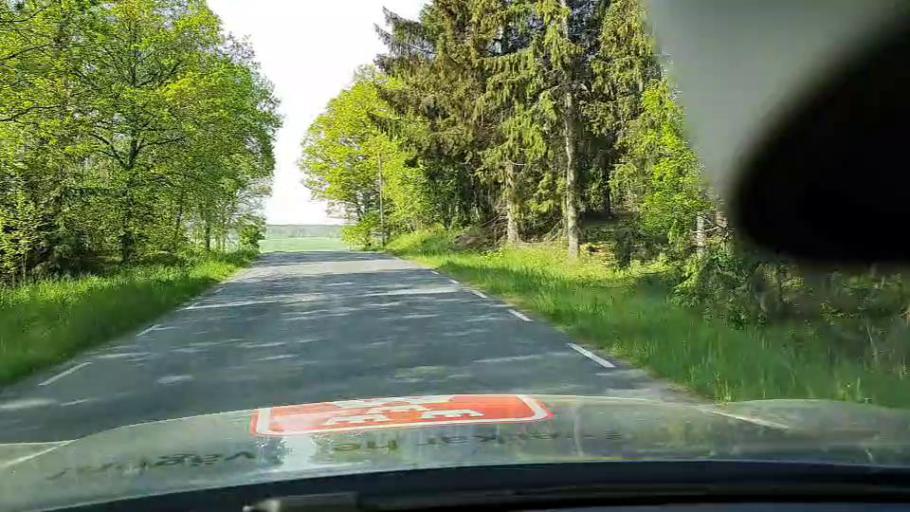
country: SE
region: Soedermanland
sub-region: Eskilstuna Kommun
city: Arla
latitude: 59.2603
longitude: 16.6539
